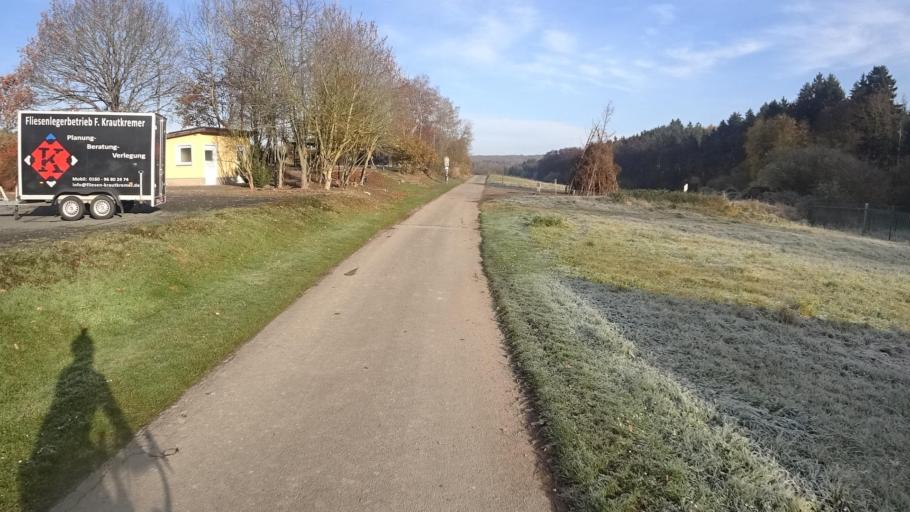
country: DE
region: Rheinland-Pfalz
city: Hausbay
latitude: 50.1088
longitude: 7.5593
